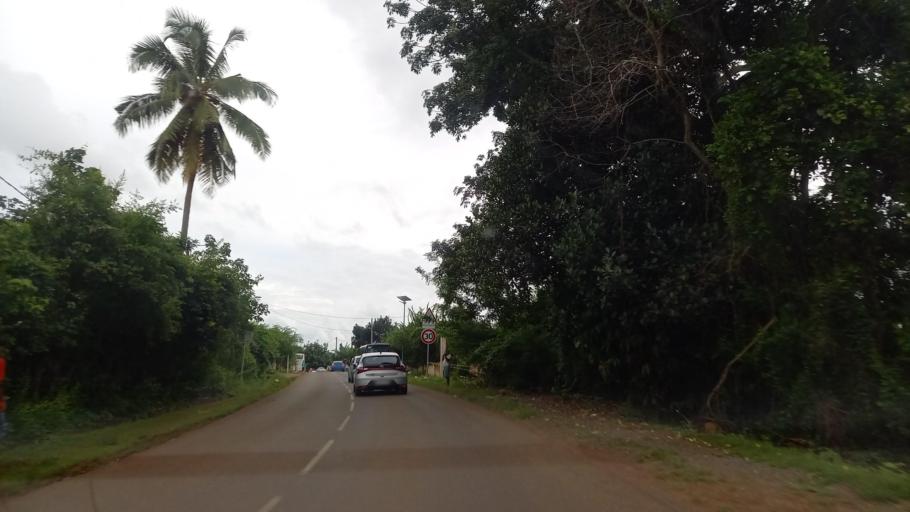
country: YT
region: Chirongui
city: Chirongui
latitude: -12.9043
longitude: 45.1506
